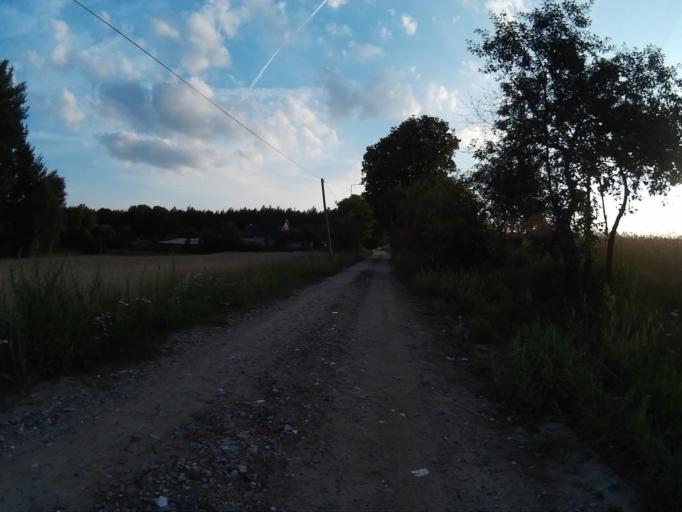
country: PL
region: Kujawsko-Pomorskie
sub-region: Powiat swiecki
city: Lniano
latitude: 53.5468
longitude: 18.1550
